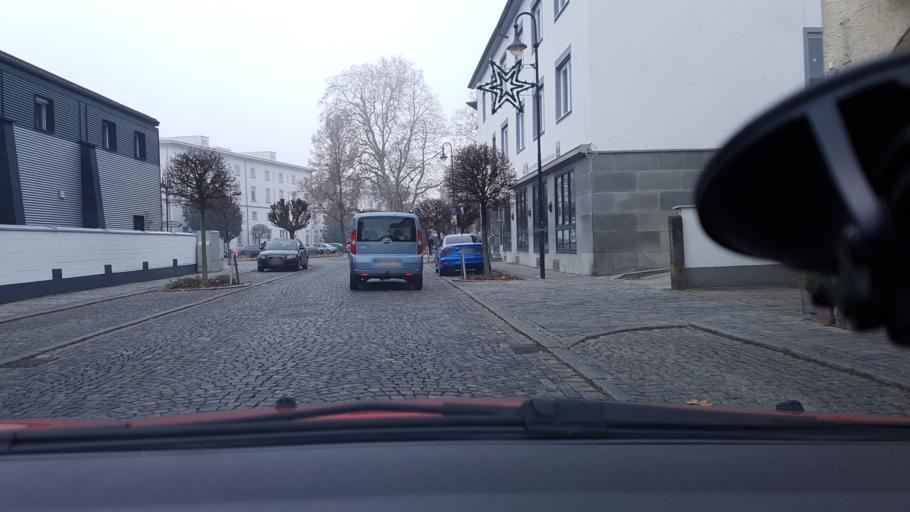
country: DE
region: Bavaria
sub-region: Lower Bavaria
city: Simbach am Inn
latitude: 48.2641
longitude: 13.0235
